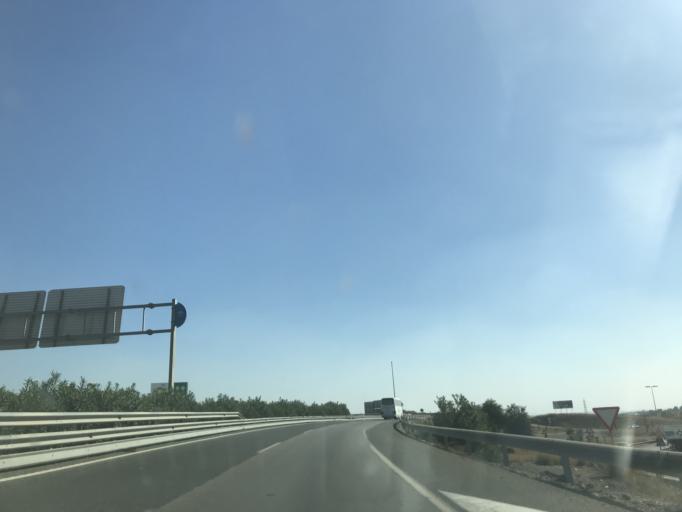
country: ES
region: Andalusia
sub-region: Provincia de Sevilla
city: Alcala de Guadaira
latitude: 37.3439
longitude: -5.8216
